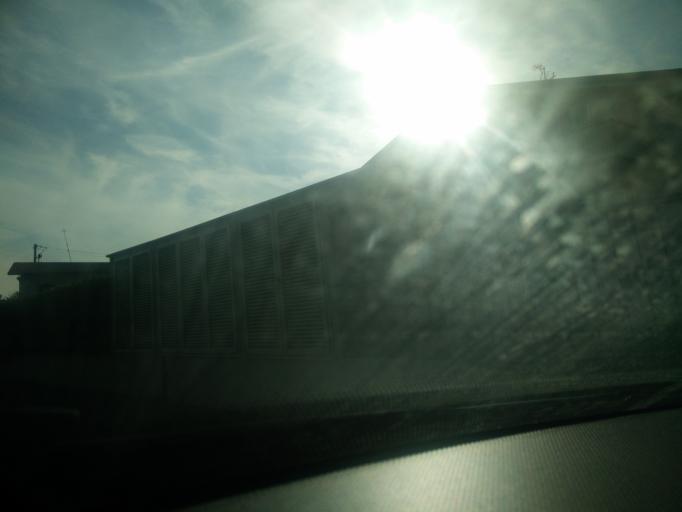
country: IT
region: Tuscany
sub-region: Provincia di Massa-Carrara
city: Massa
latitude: 44.0235
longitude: 10.1226
